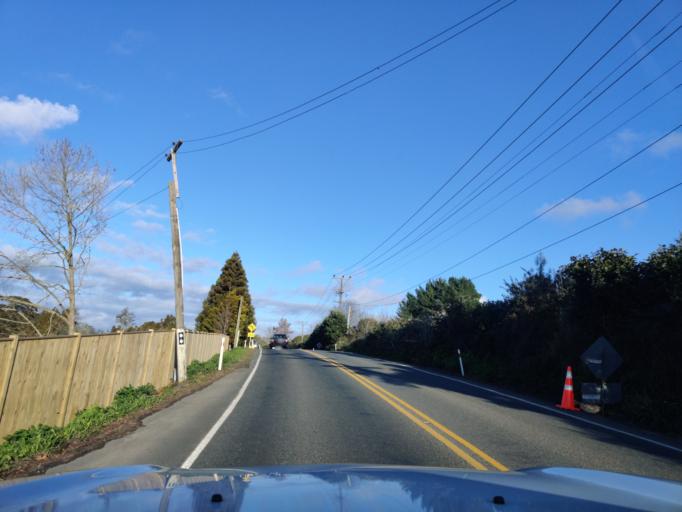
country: NZ
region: Auckland
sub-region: Auckland
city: Red Hill
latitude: -36.9715
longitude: 174.9860
